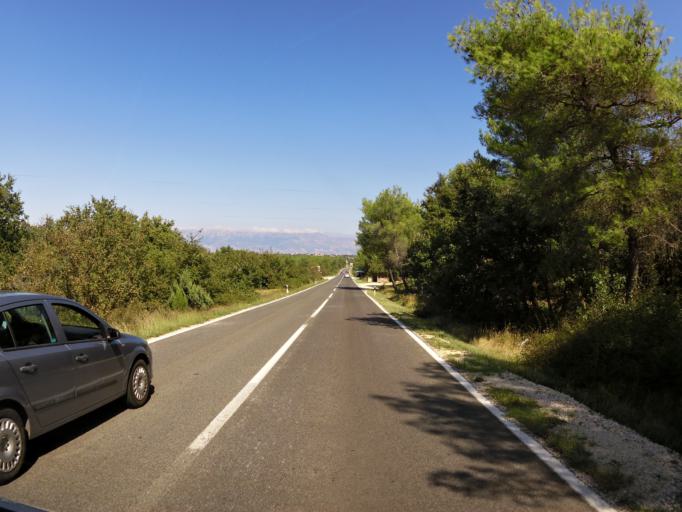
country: HR
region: Zadarska
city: Policnik
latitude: 44.1635
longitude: 15.3510
